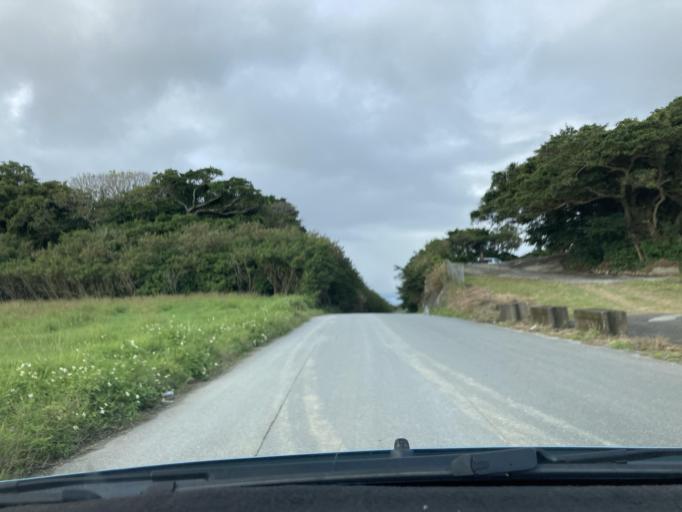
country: JP
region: Okinawa
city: Itoman
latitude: 26.1215
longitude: 127.6864
